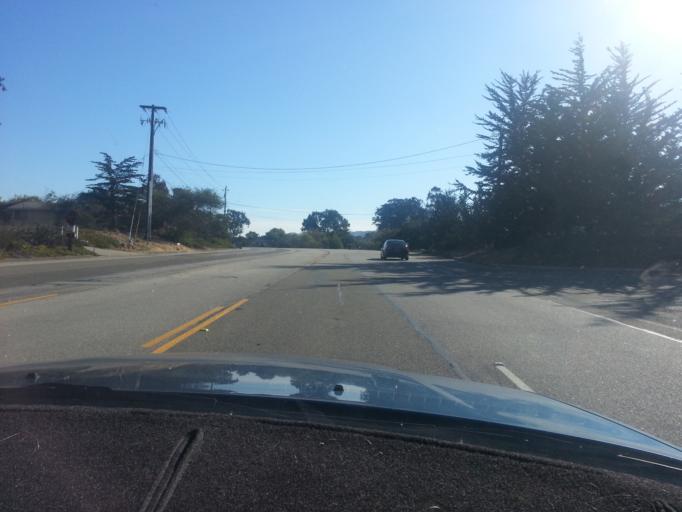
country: US
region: California
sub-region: San Luis Obispo County
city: Los Osos
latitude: 35.3093
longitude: -120.8241
